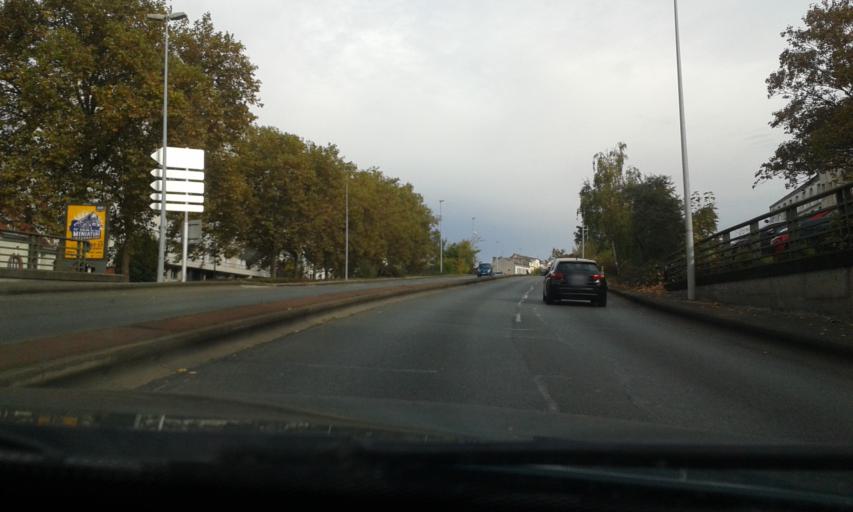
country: FR
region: Centre
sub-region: Departement du Loiret
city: Orleans
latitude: 47.9024
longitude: 1.8938
